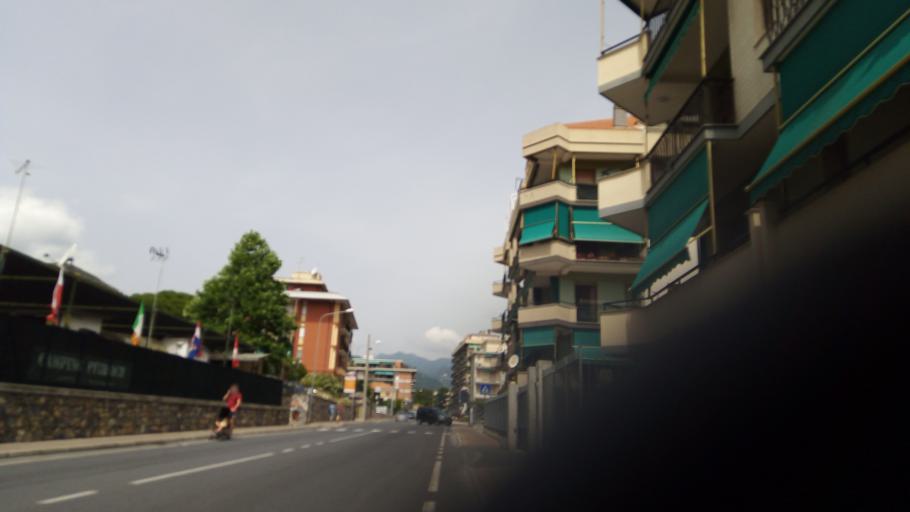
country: IT
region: Liguria
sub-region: Provincia di Savona
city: Borghetto Santo Spirito
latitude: 44.1110
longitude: 8.2391
